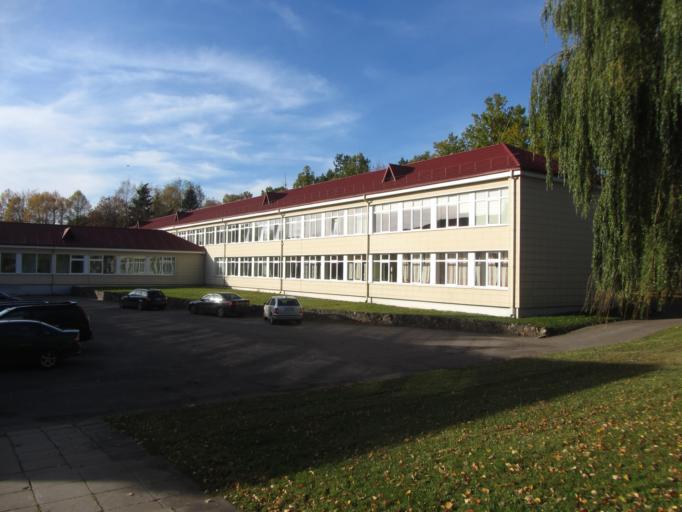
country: LT
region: Vilnius County
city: Elektrenai
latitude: 54.7849
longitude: 24.6614
